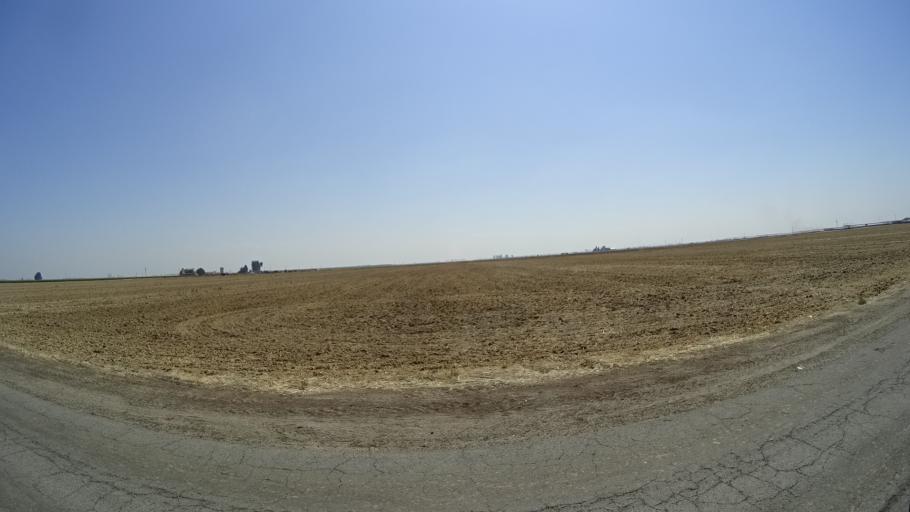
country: US
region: California
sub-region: Tulare County
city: London
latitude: 36.4056
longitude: -119.5288
